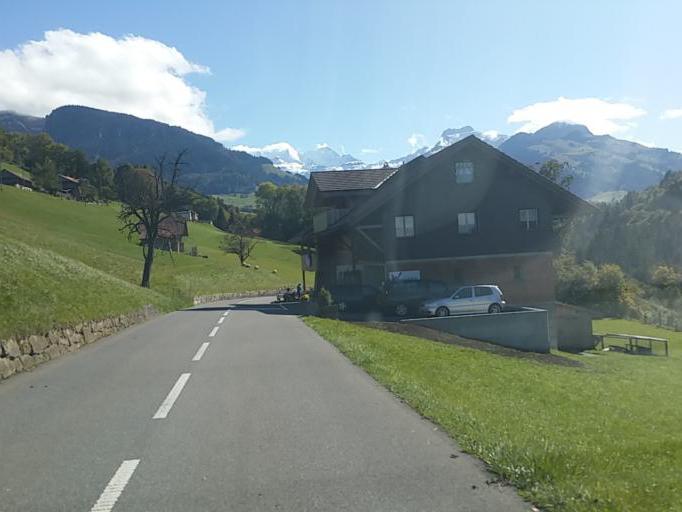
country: CH
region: Bern
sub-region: Frutigen-Niedersimmental District
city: Aeschi
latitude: 46.6492
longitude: 7.6888
